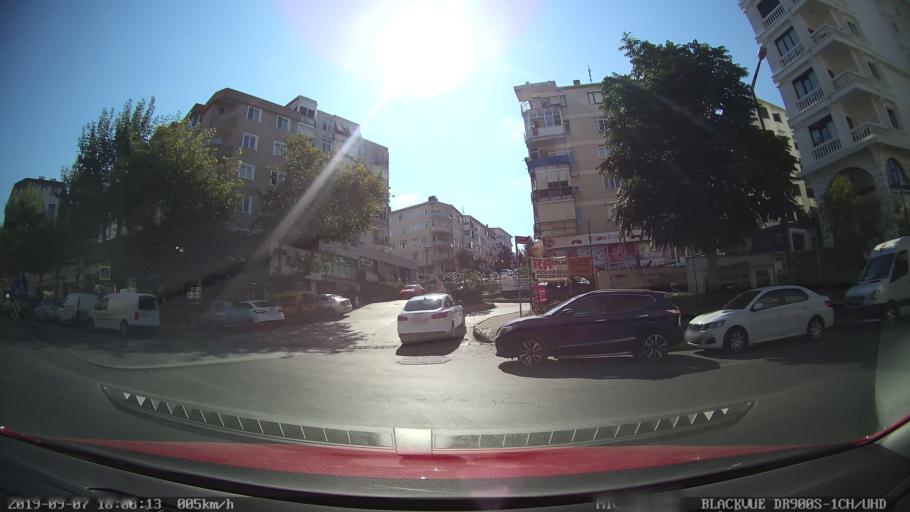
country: TR
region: Istanbul
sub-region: Atasehir
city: Atasehir
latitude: 40.9479
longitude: 29.1133
